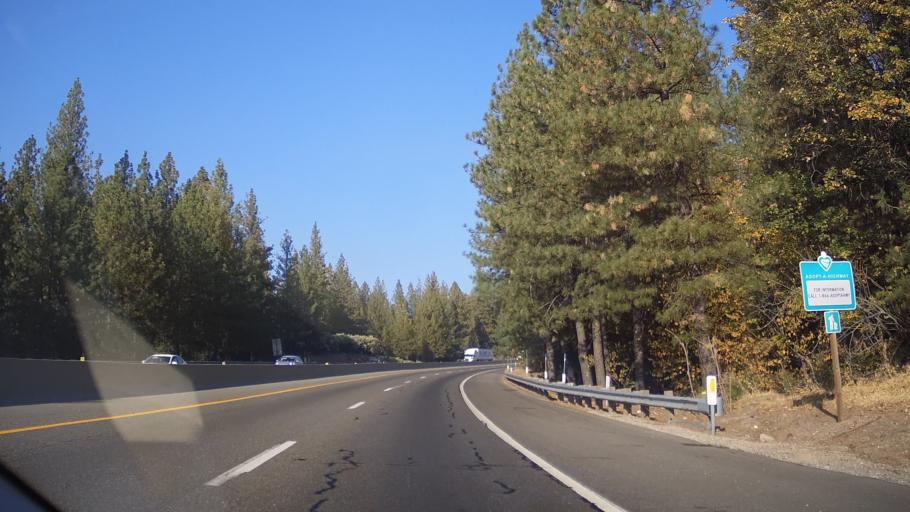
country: US
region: California
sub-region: Placer County
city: Colfax
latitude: 39.1670
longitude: -120.8754
